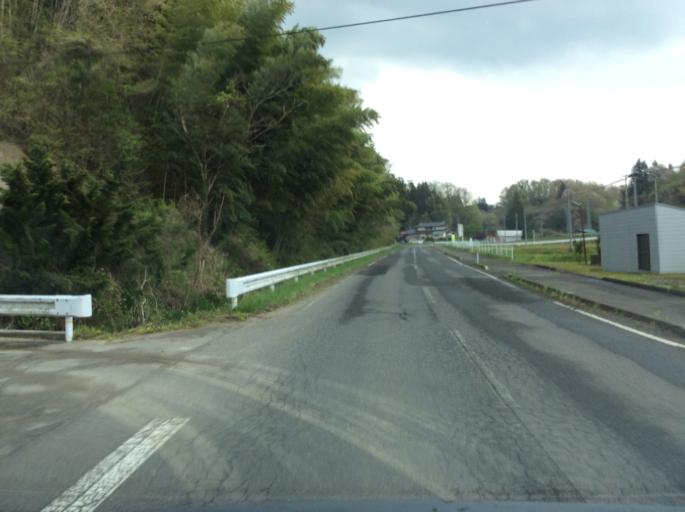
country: JP
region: Fukushima
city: Funehikimachi-funehiki
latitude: 37.4070
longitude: 140.5408
